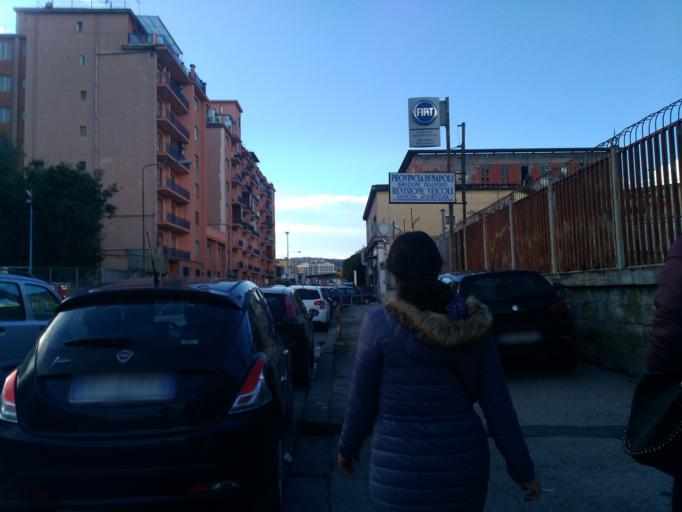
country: IT
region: Campania
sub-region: Provincia di Napoli
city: Napoli
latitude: 40.8497
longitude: 14.2803
